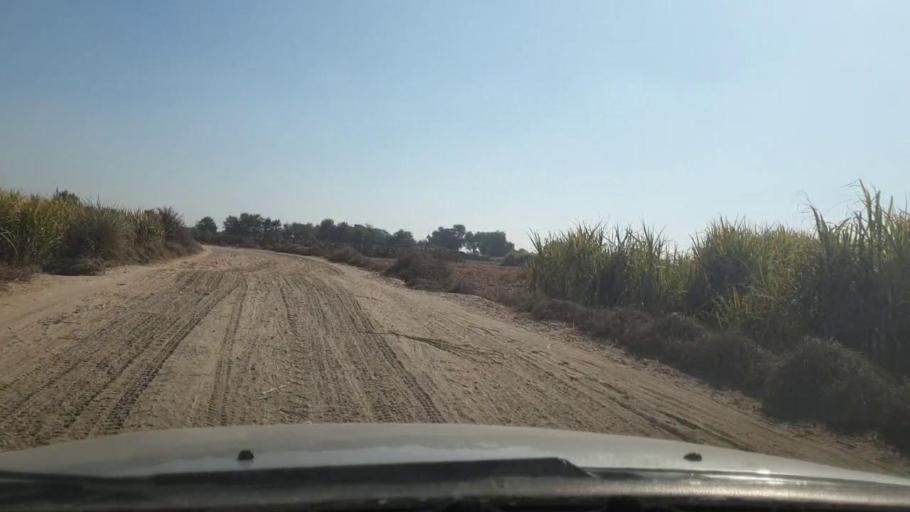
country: PK
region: Sindh
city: Ghotki
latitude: 28.0242
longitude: 69.2200
